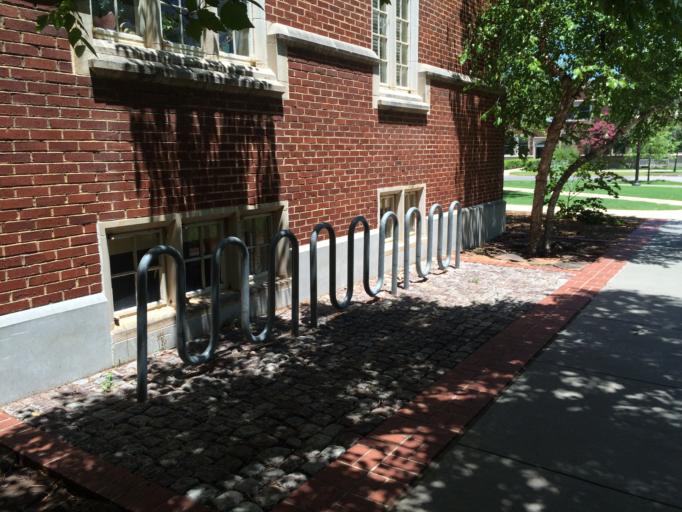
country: US
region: Oklahoma
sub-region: Cleveland County
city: Norman
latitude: 35.2088
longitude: -97.4443
